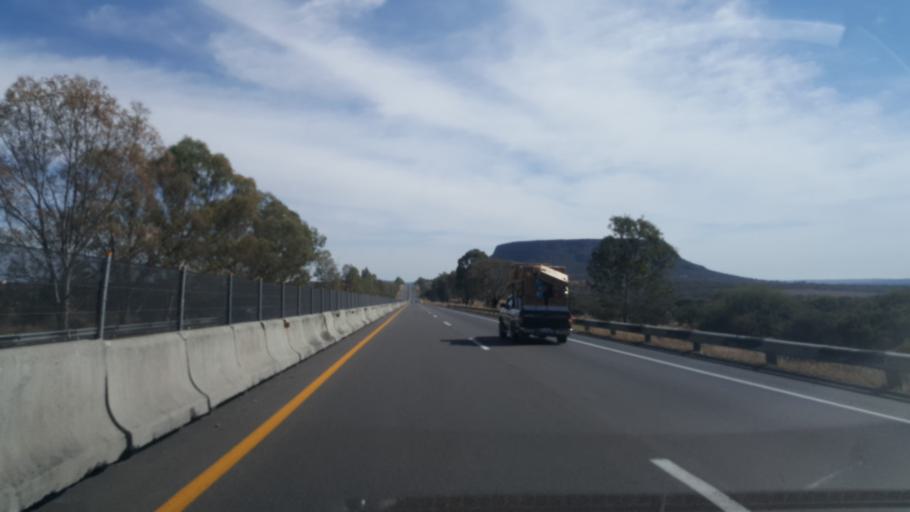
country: MX
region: Jalisco
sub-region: Lagos de Moreno
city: Cristeros [Fraccionamiento]
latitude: 21.3059
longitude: -102.0260
